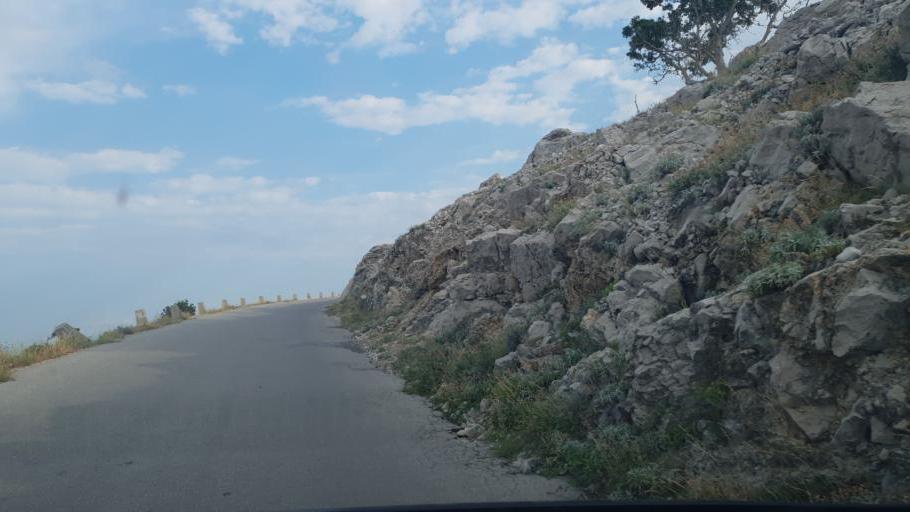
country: HR
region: Primorsko-Goranska
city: Omisalj
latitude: 45.2271
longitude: 14.5821
